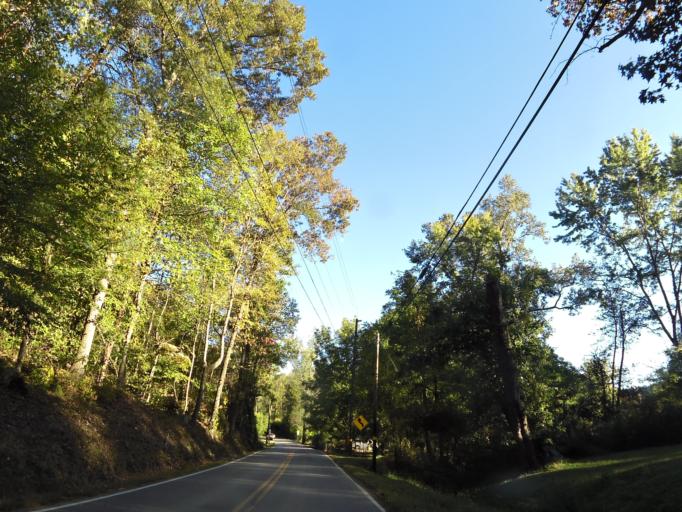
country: US
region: Tennessee
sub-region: Grainger County
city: Rutledge
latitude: 36.2406
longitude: -83.6207
